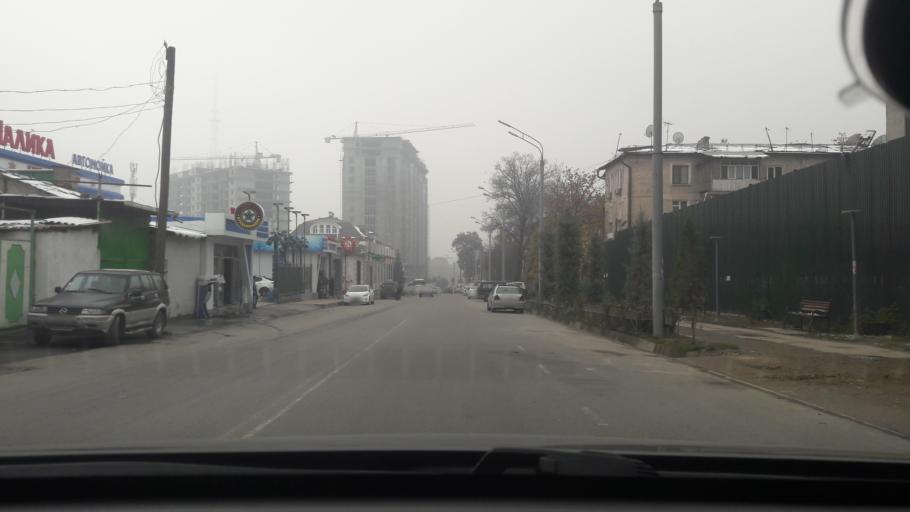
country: TJ
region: Dushanbe
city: Dushanbe
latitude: 38.5778
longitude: 68.8002
